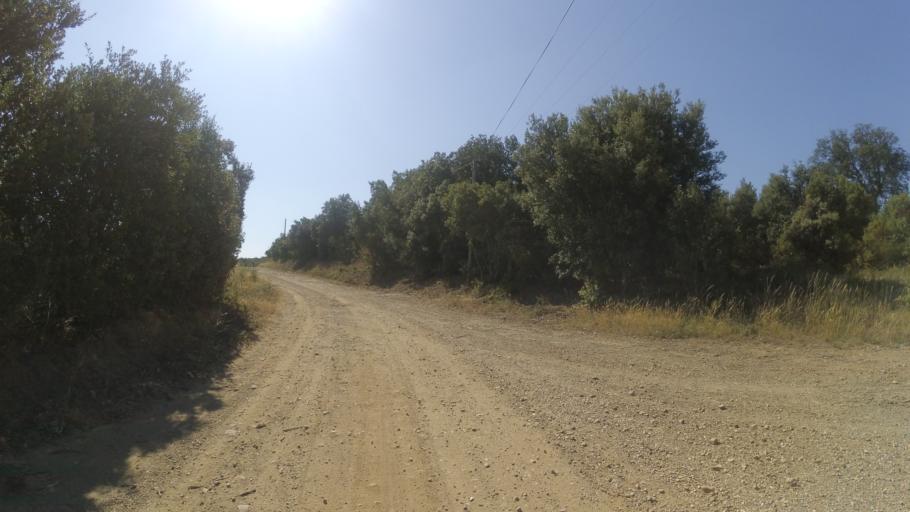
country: FR
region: Languedoc-Roussillon
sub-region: Departement des Pyrenees-Orientales
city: Millas
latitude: 42.6167
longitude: 2.6773
